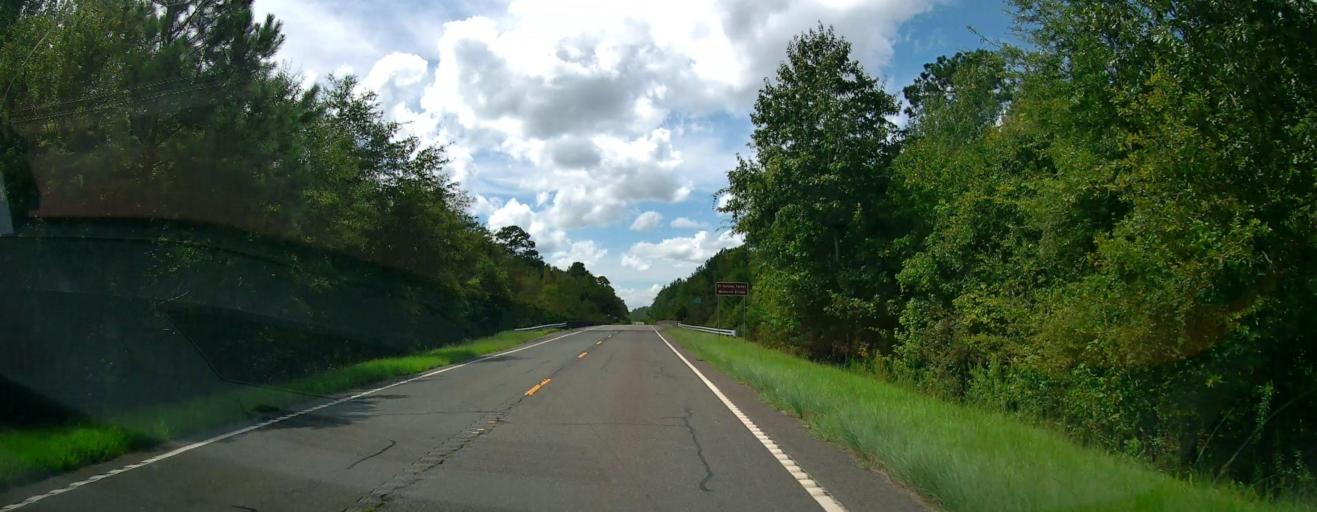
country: US
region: Georgia
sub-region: Macon County
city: Marshallville
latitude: 32.4332
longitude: -84.0331
